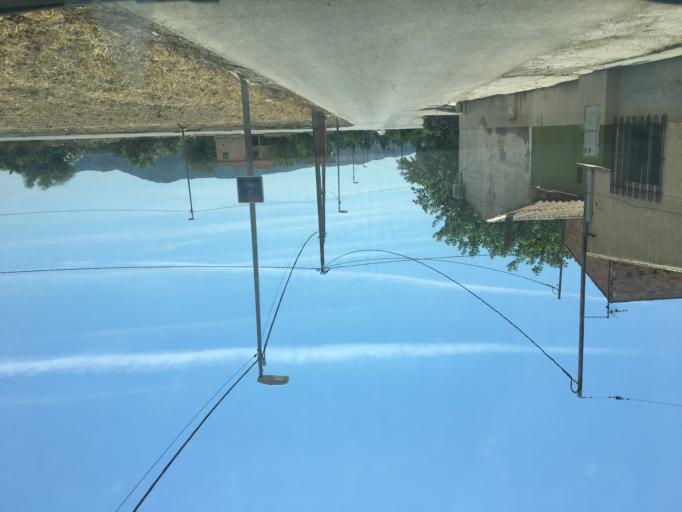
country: ES
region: Murcia
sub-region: Murcia
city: Santomera
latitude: 38.0248
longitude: -1.0597
